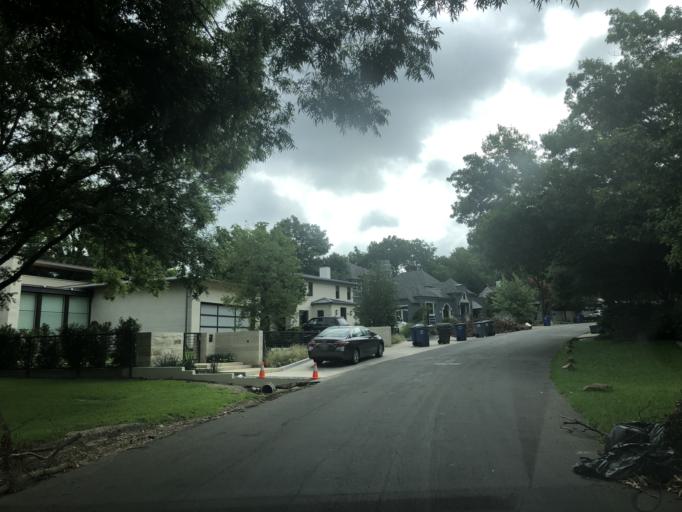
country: US
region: Texas
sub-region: Dallas County
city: University Park
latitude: 32.8592
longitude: -96.8245
